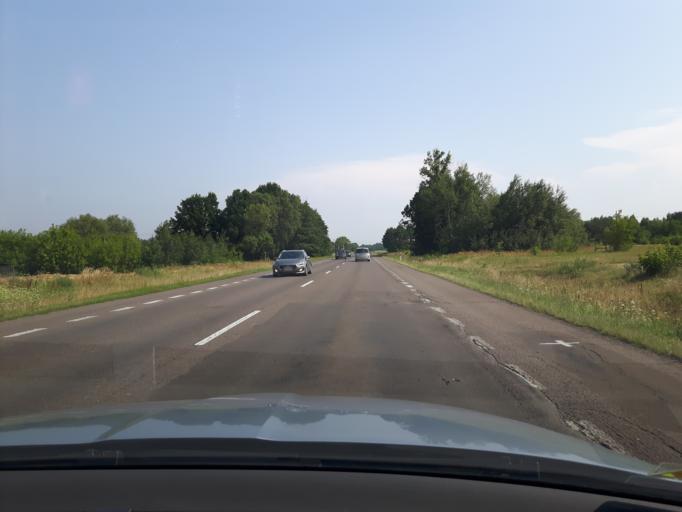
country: PL
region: Masovian Voivodeship
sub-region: Powiat ciechanowski
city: Glinojeck
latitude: 52.7658
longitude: 20.2998
